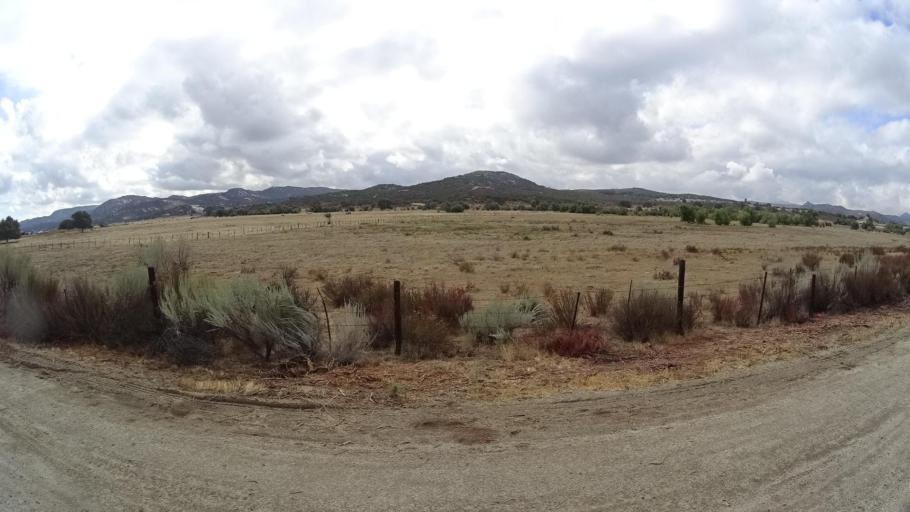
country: US
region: California
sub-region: San Diego County
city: Campo
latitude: 32.6294
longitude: -116.4595
